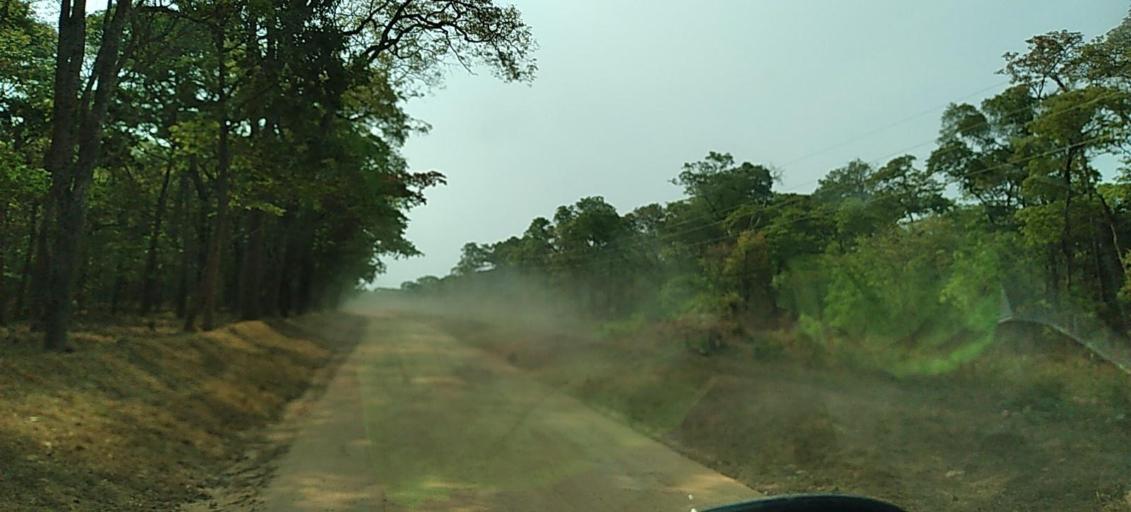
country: ZM
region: North-Western
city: Solwezi
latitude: -12.6895
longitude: 26.3988
